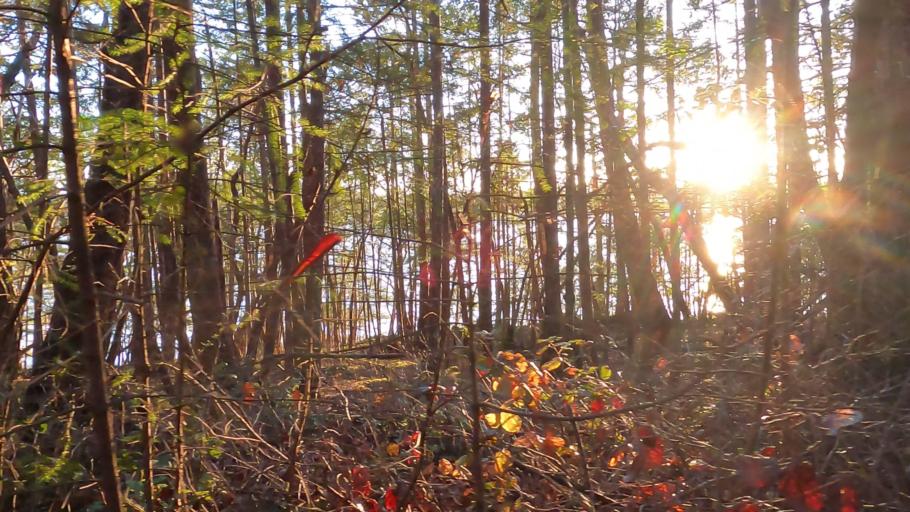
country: CA
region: British Columbia
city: North Cowichan
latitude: 48.9506
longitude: -123.5650
